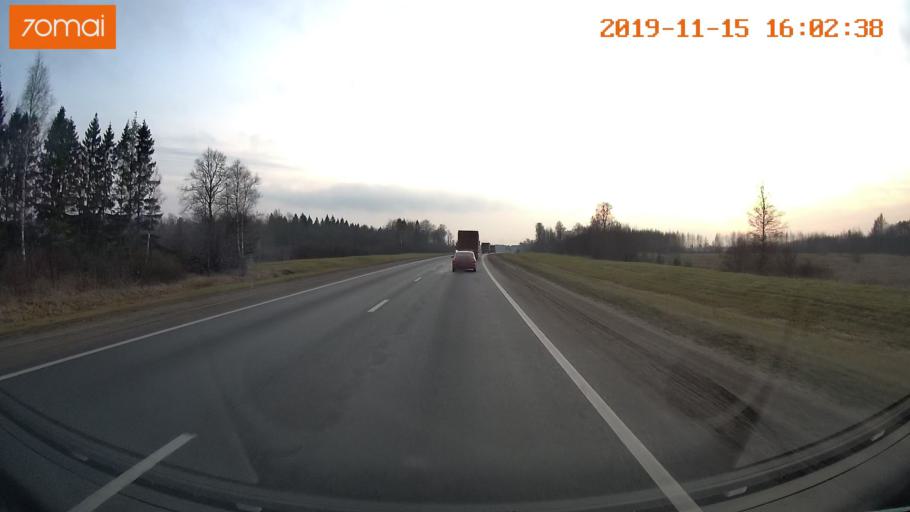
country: RU
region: Jaroslavl
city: Yaroslavl
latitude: 57.7691
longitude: 39.9228
